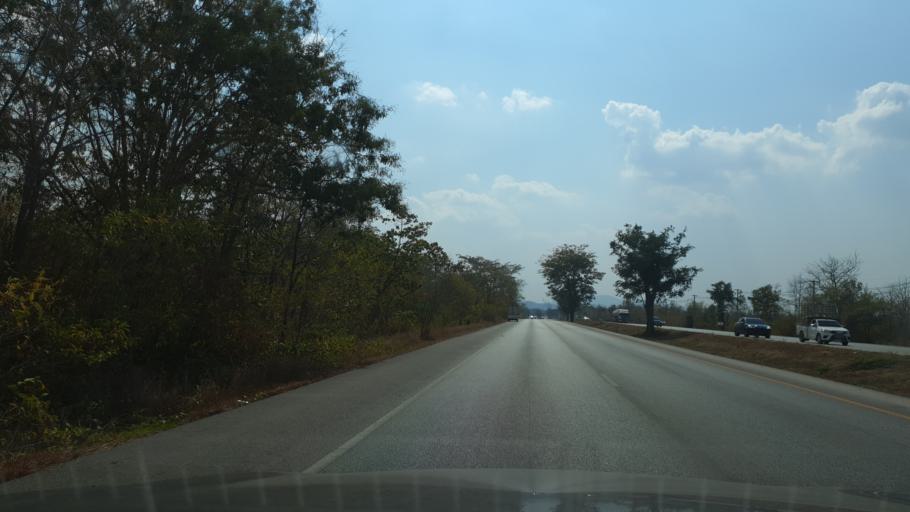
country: TH
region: Lampang
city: Mae Phrik
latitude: 17.4328
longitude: 99.1584
